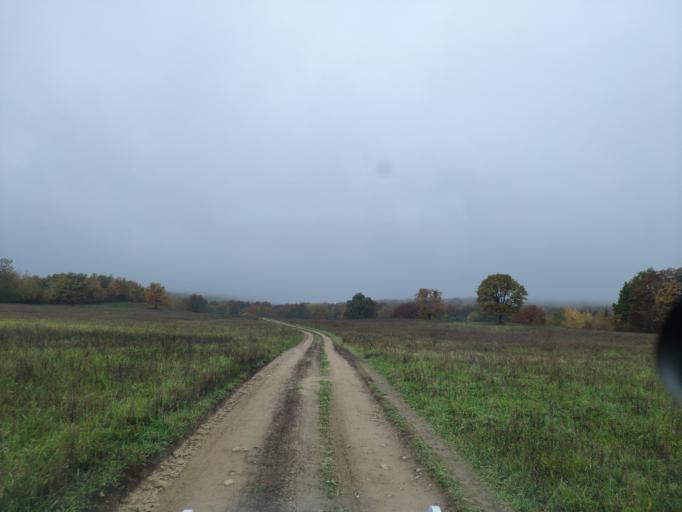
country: SK
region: Kosicky
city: Moldava nad Bodvou
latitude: 48.7122
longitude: 21.0145
